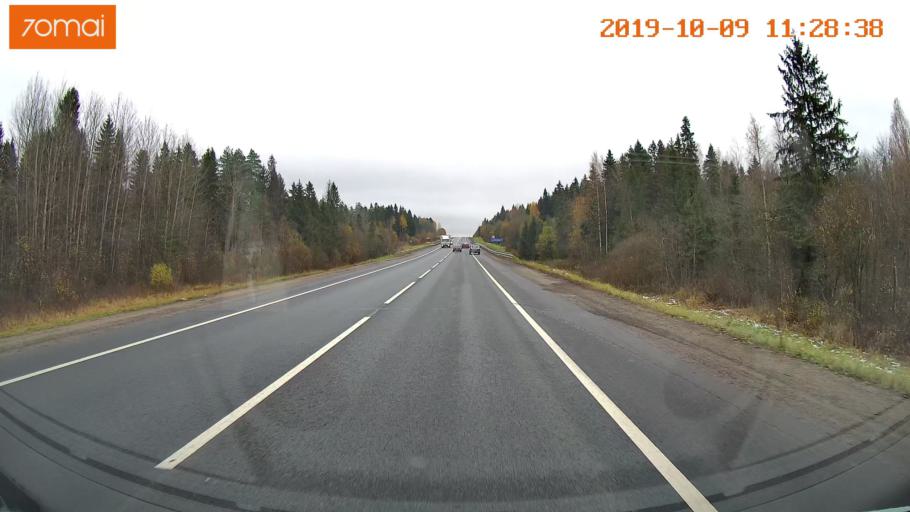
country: RU
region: Vologda
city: Vologda
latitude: 59.0669
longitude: 40.0413
